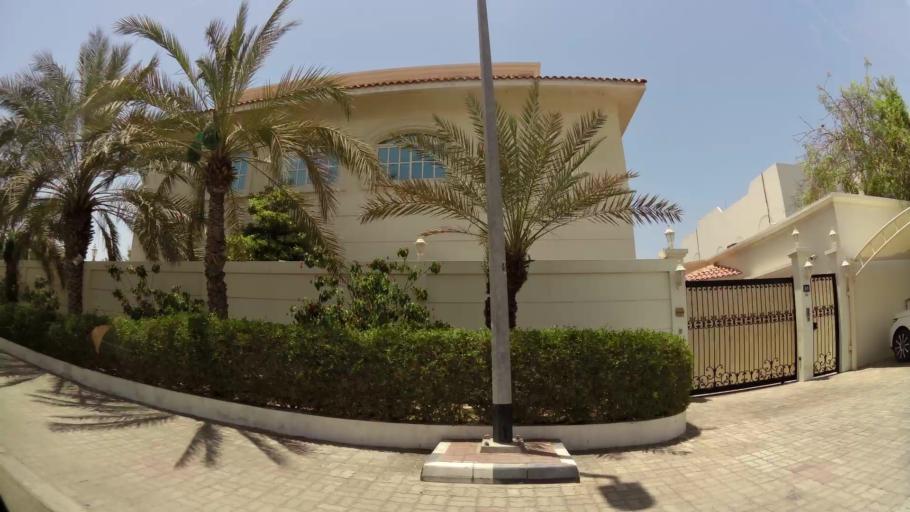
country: AE
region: Dubai
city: Dubai
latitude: 25.2203
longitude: 55.2564
